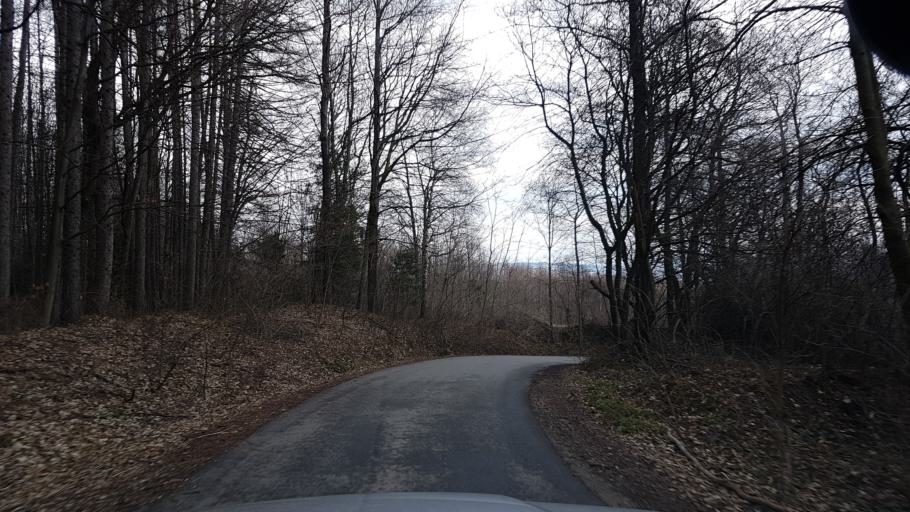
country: PL
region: Lesser Poland Voivodeship
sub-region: Powiat nowosadecki
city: Stary Sacz
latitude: 49.5372
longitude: 20.6362
